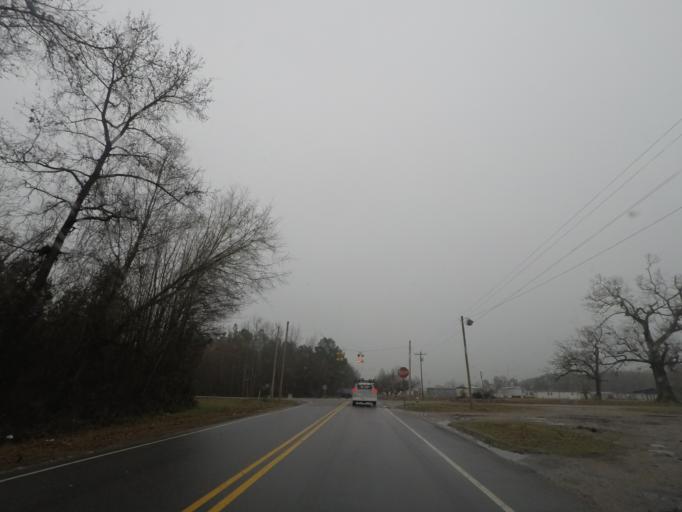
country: US
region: North Carolina
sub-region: Scotland County
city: Laurinburg
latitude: 34.7990
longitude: -79.4327
